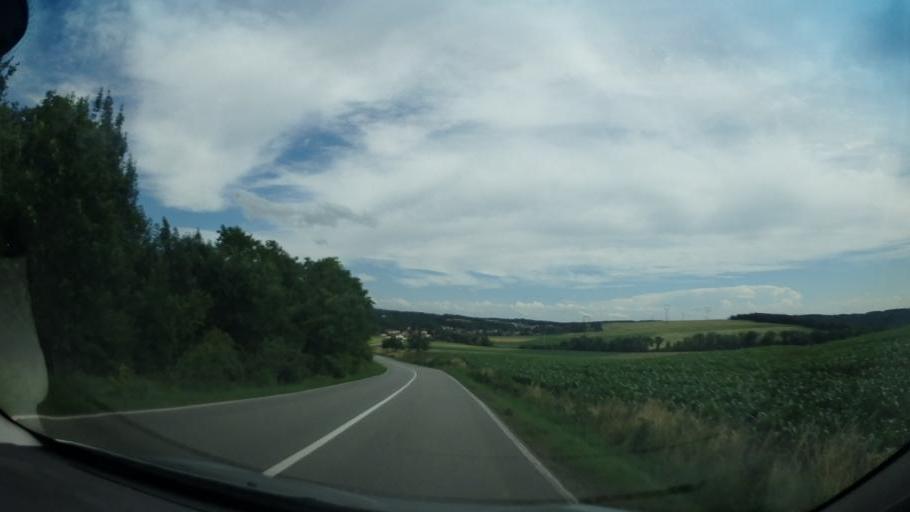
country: CZ
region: South Moravian
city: Zbysov
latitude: 49.1528
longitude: 16.3790
